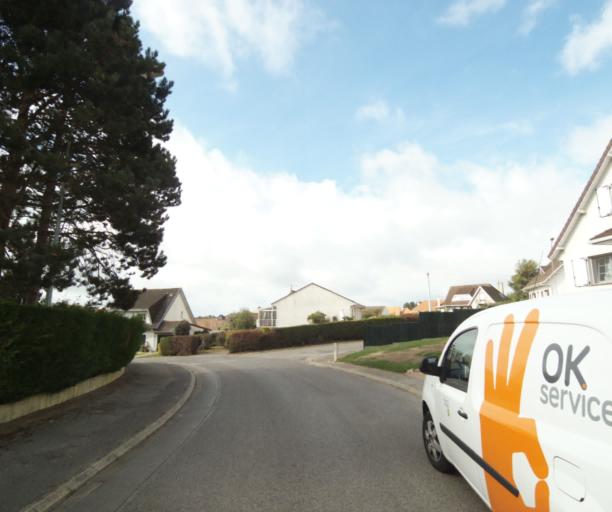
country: FR
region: Nord-Pas-de-Calais
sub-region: Departement du Pas-de-Calais
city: Etaples
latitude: 50.5273
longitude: 1.6327
